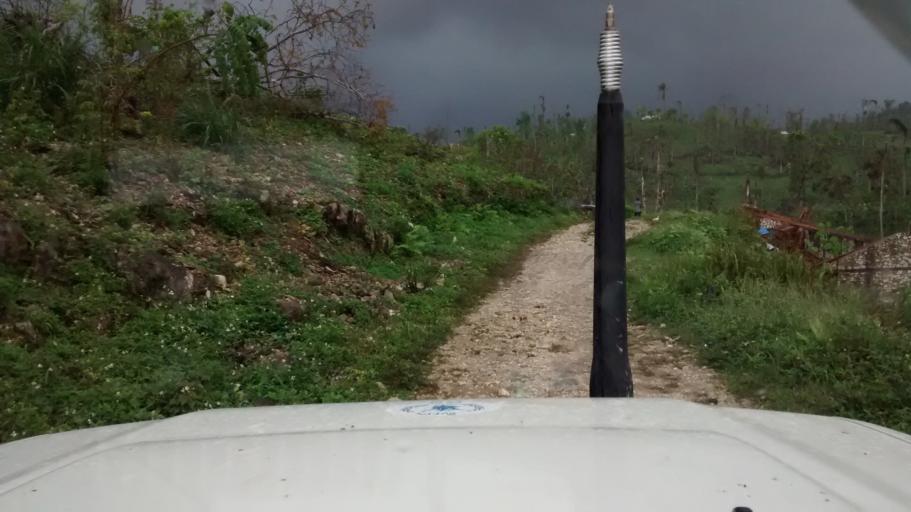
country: HT
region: Grandans
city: Moron
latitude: 18.5319
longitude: -74.1571
